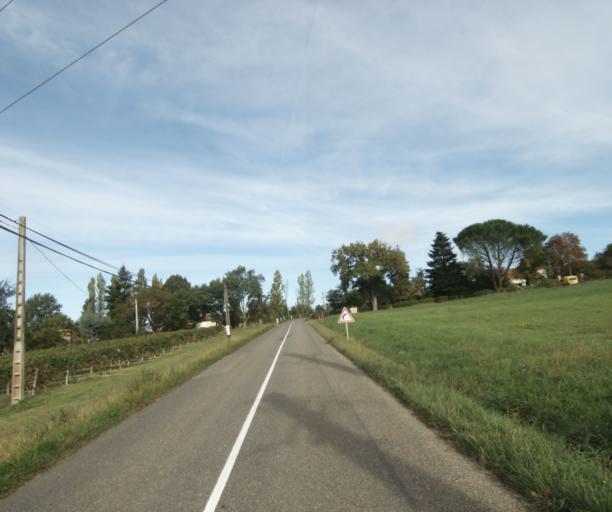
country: FR
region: Midi-Pyrenees
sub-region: Departement du Gers
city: Eauze
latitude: 43.8731
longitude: 0.1225
